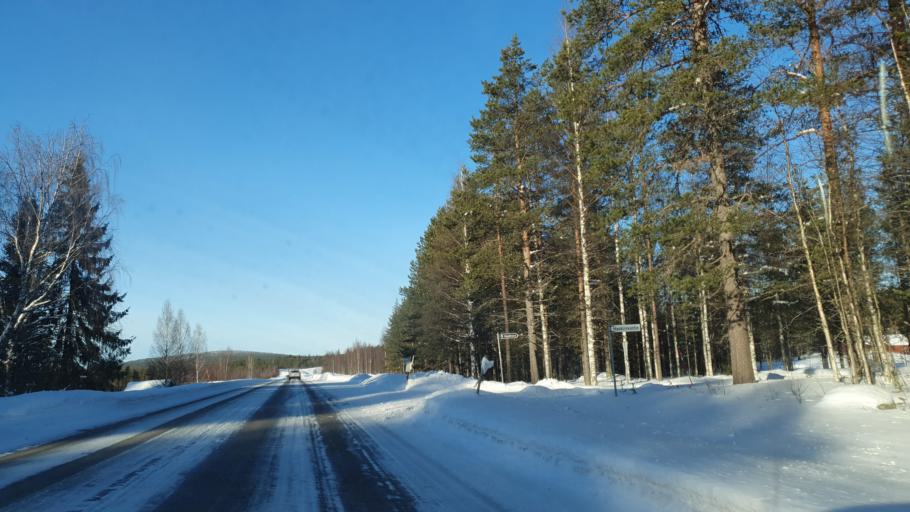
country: FI
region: Lapland
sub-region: Torniolaakso
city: Pello
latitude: 67.0152
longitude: 24.0494
